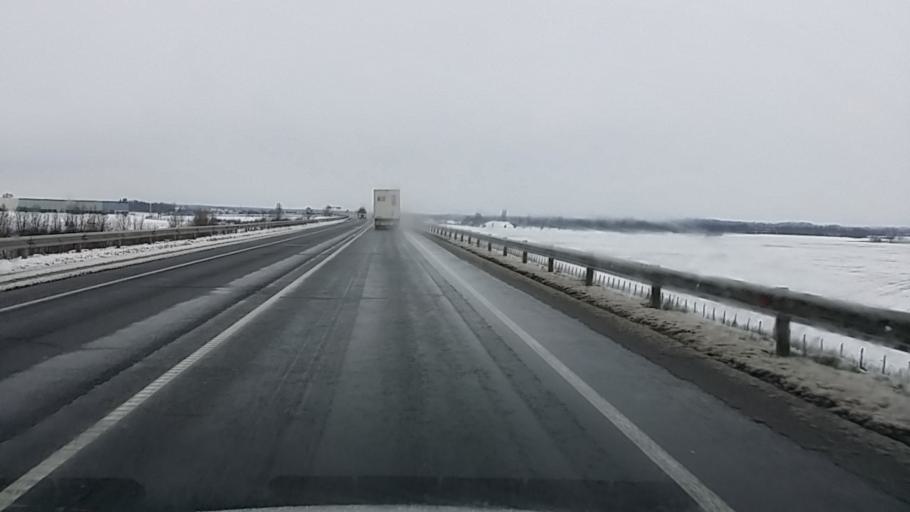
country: HU
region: Gyor-Moson-Sopron
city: Mosonmagyarovar
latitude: 47.8980
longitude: 17.1823
